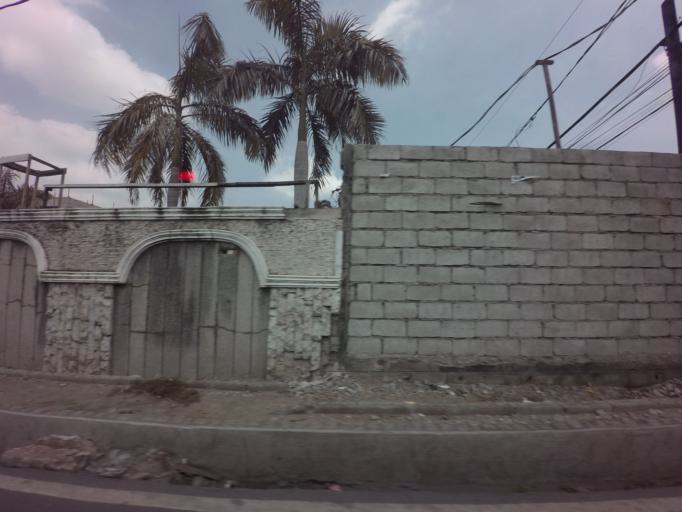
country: PH
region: Calabarzon
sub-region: Province of Rizal
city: Taguig
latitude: 14.4694
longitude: 121.0573
